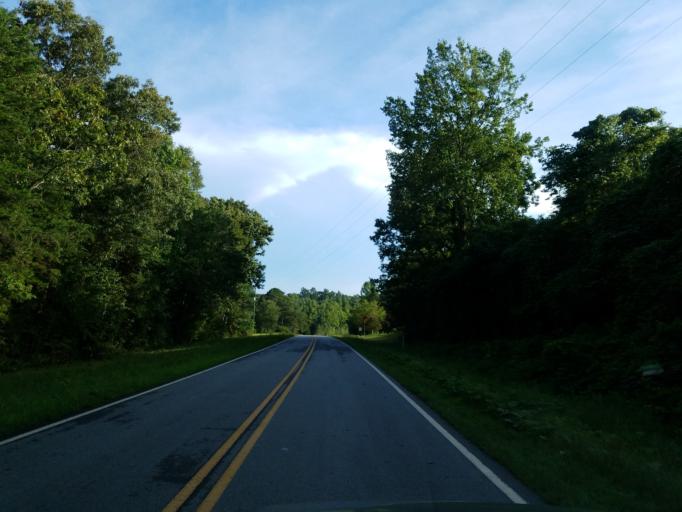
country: US
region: Georgia
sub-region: White County
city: Cleveland
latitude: 34.6049
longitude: -83.8603
